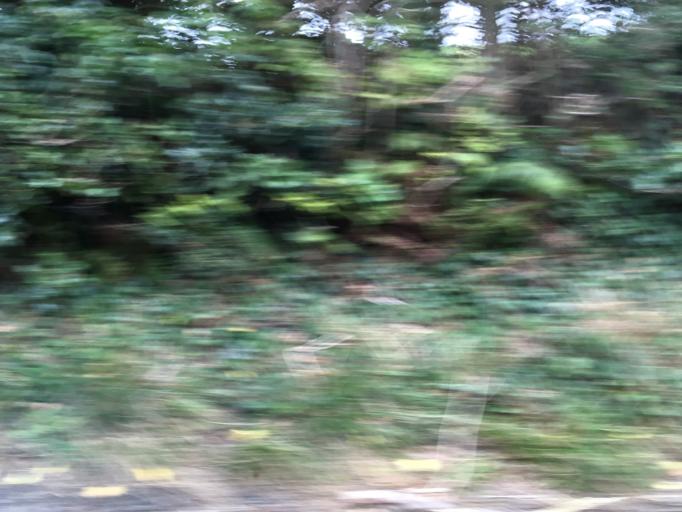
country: IE
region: Leinster
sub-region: Wicklow
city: Rathnew
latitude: 52.9202
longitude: -6.1003
